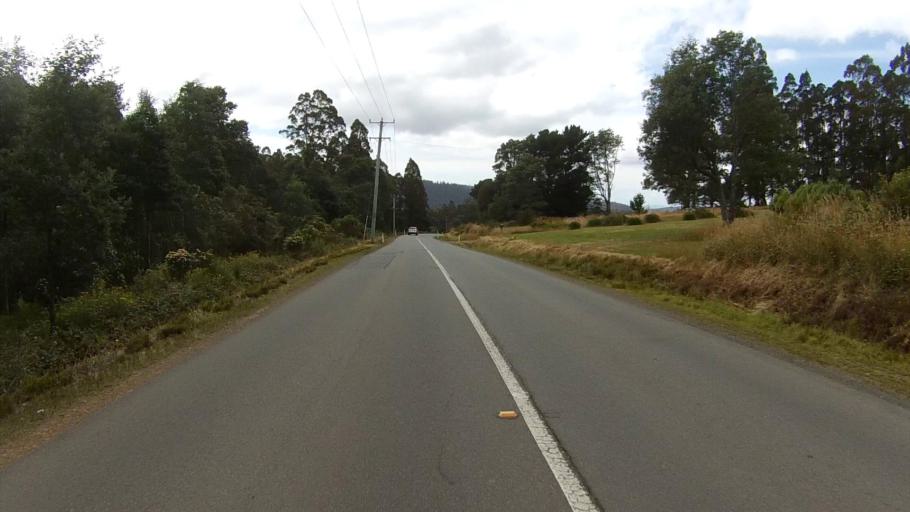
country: AU
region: Tasmania
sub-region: Kingborough
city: Kettering
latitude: -43.1141
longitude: 147.1924
